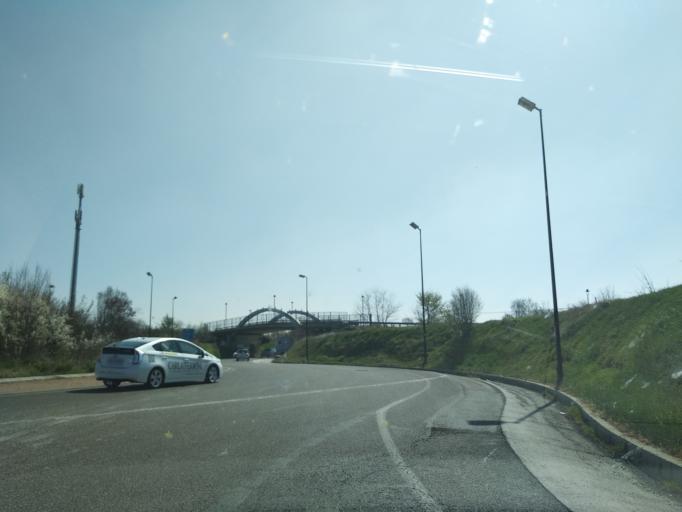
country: IT
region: Emilia-Romagna
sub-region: Provincia di Reggio Emilia
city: Albinea
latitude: 44.6640
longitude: 10.6097
